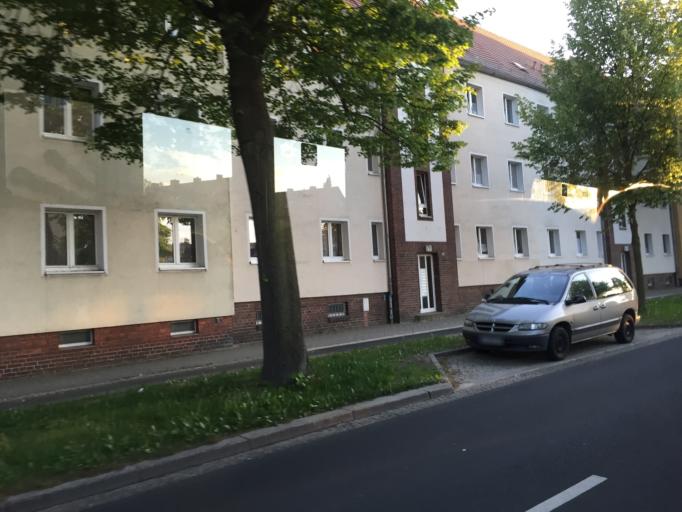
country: DE
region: Saxony
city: Goerlitz
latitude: 51.1461
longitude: 14.9622
